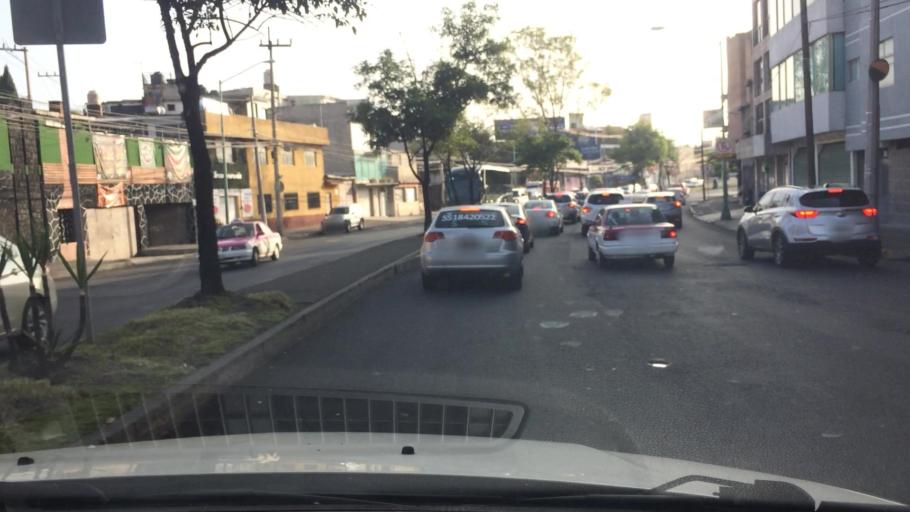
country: MX
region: Mexico City
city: Tlalpan
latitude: 19.3025
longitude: -99.1610
